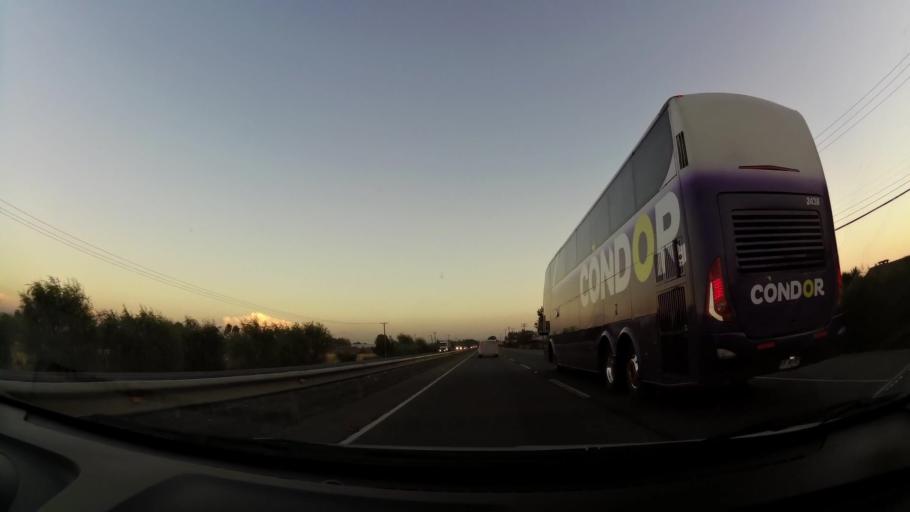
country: CL
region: Maule
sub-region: Provincia de Linares
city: Linares
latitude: -35.8170
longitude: -71.6447
